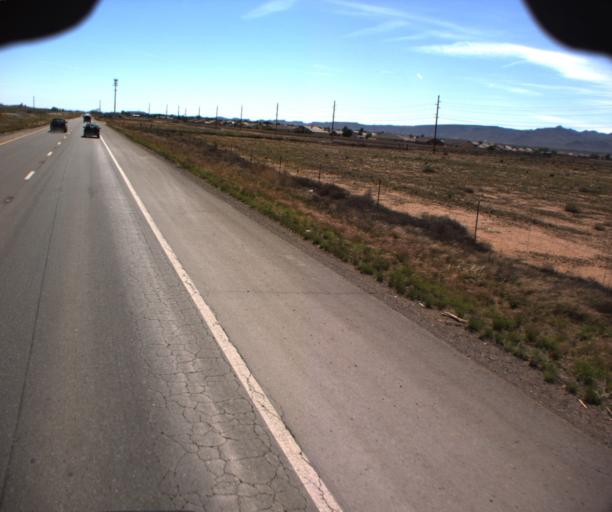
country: US
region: Arizona
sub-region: Mohave County
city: New Kingman-Butler
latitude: 35.2693
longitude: -113.9610
